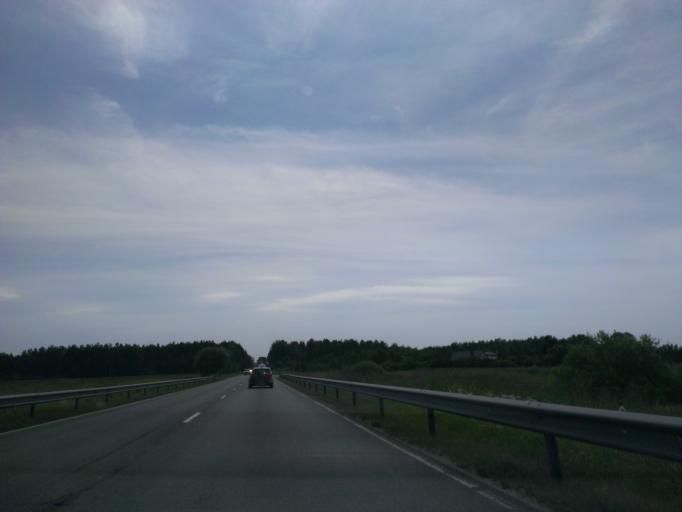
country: LV
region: Salaspils
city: Salaspils
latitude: 56.8981
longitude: 24.4067
